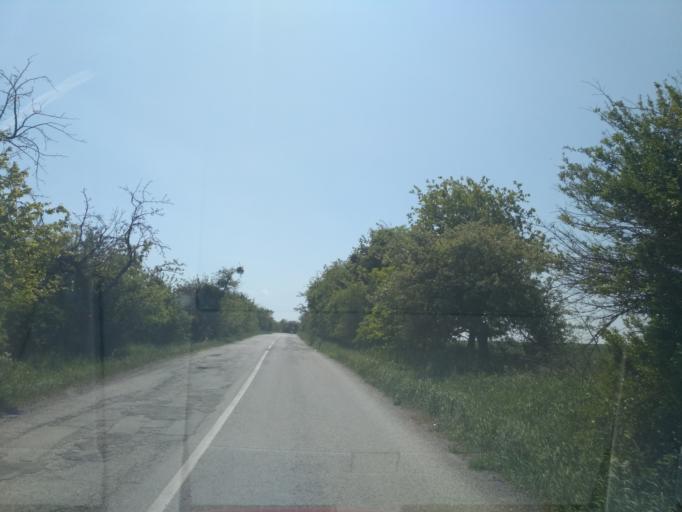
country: SK
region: Kosicky
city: Kosice
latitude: 48.8069
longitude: 21.3993
